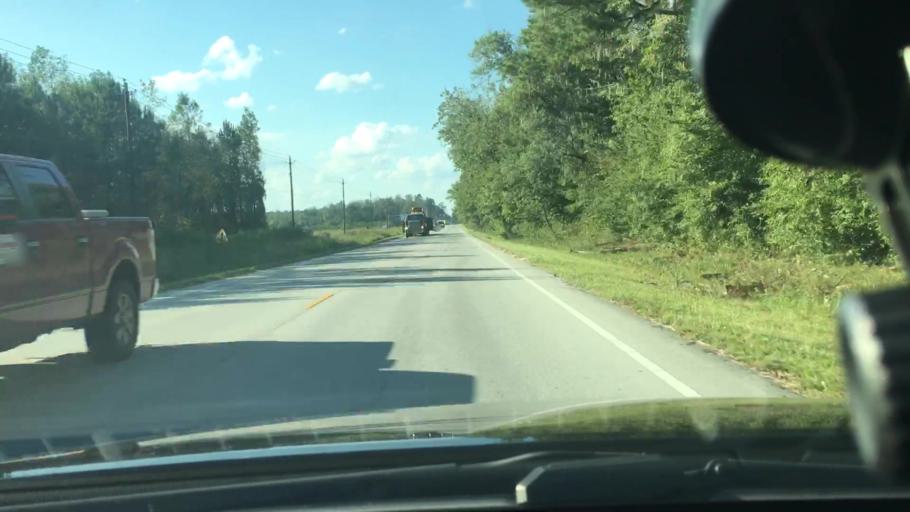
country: US
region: North Carolina
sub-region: Craven County
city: Vanceboro
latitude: 35.2458
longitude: -77.0846
